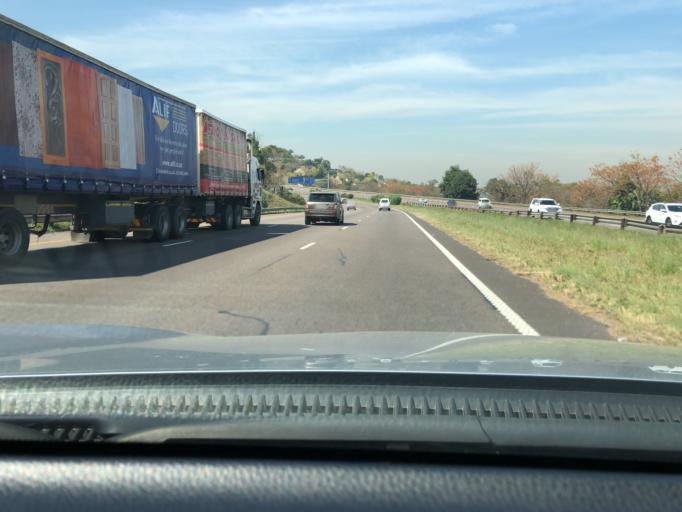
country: ZA
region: KwaZulu-Natal
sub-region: eThekwini Metropolitan Municipality
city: Berea
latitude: -29.8351
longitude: 30.8534
